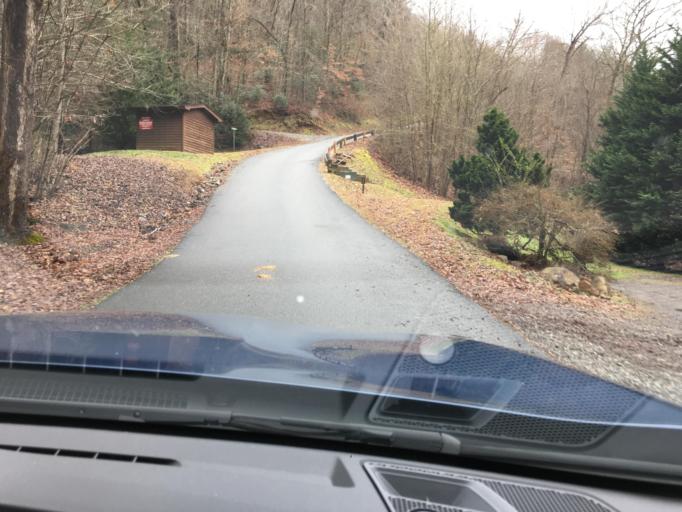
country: US
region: North Carolina
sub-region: Cherokee County
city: Murphy
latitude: 35.1599
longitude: -83.9408
